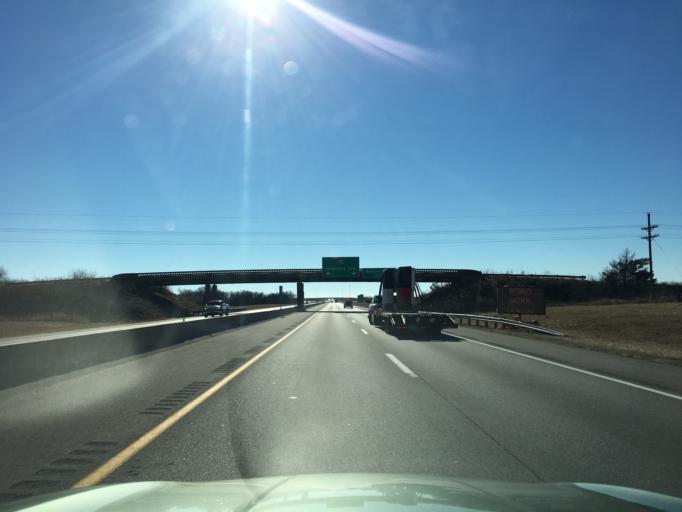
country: US
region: Kansas
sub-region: Sumner County
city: Wellington
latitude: 37.2916
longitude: -97.3403
